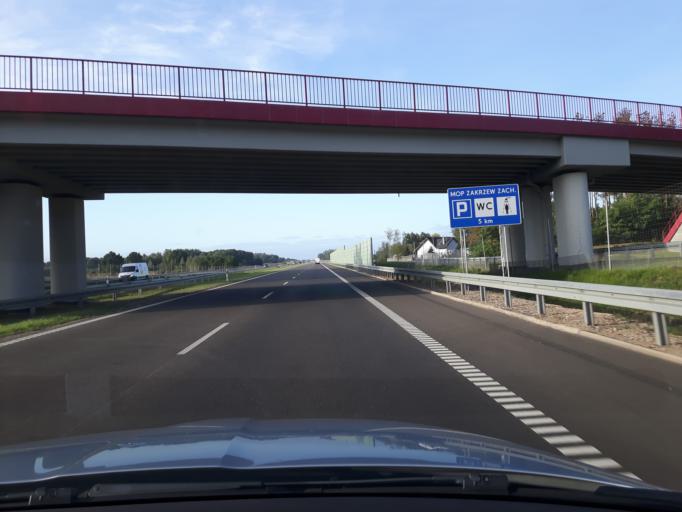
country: PL
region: Masovian Voivodeship
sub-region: Powiat radomski
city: Jedlinsk
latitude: 51.4884
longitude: 21.0692
